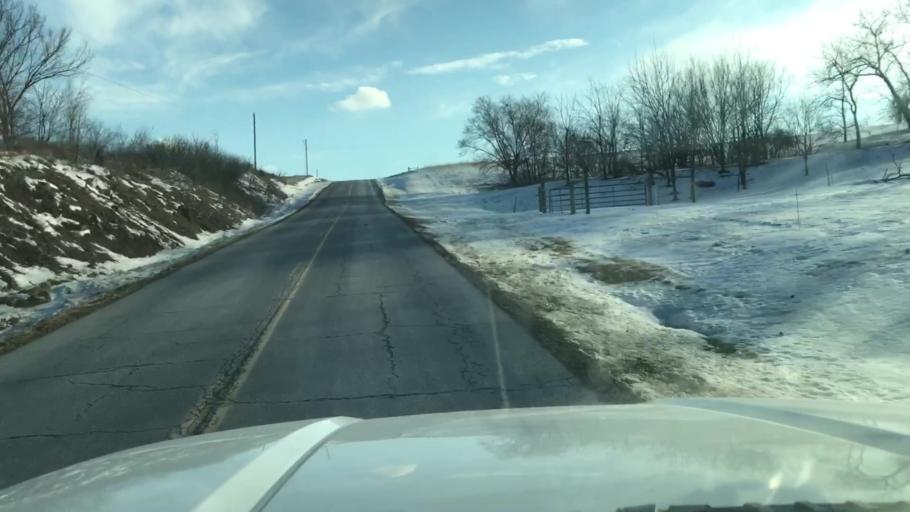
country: US
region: Missouri
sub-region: Holt County
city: Oregon
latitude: 40.0706
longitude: -94.9747
